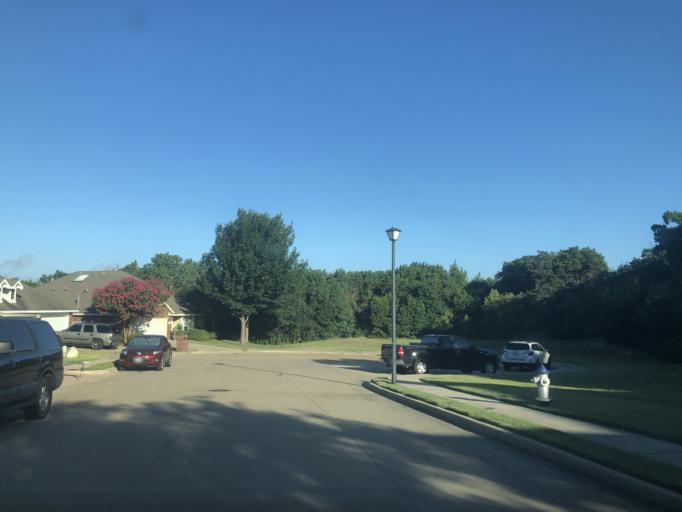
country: US
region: Texas
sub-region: Dallas County
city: Duncanville
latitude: 32.6601
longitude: -96.9466
